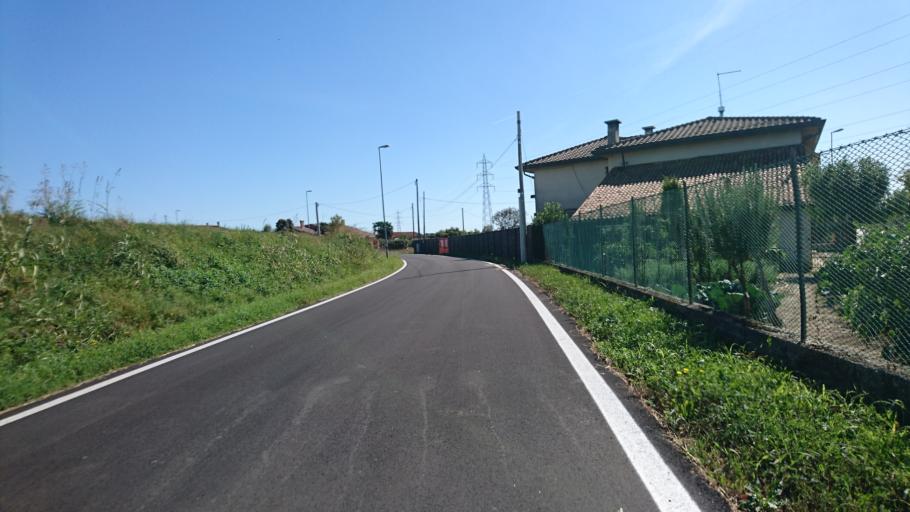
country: IT
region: Veneto
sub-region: Provincia di Venezia
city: Fiesso
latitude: 45.4109
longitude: 12.0592
